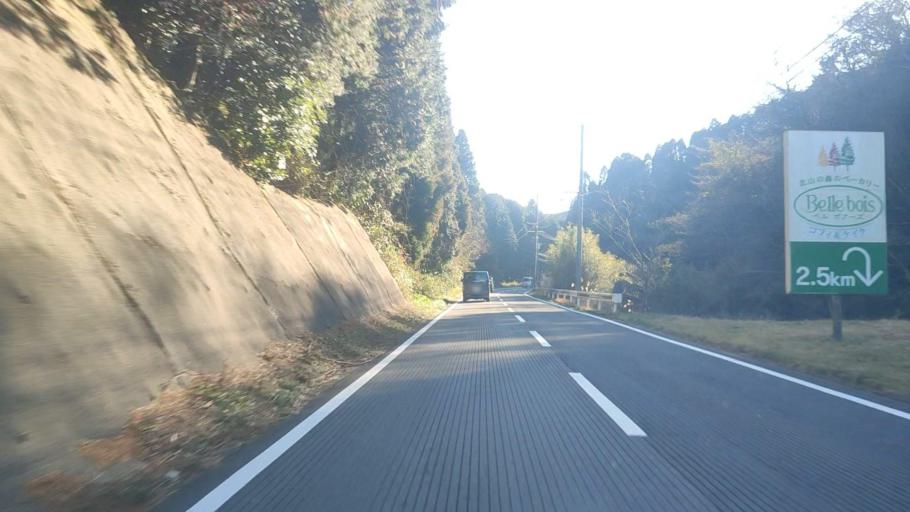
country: JP
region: Saga Prefecture
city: Kanzakimachi-kanzaki
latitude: 33.4188
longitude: 130.2793
